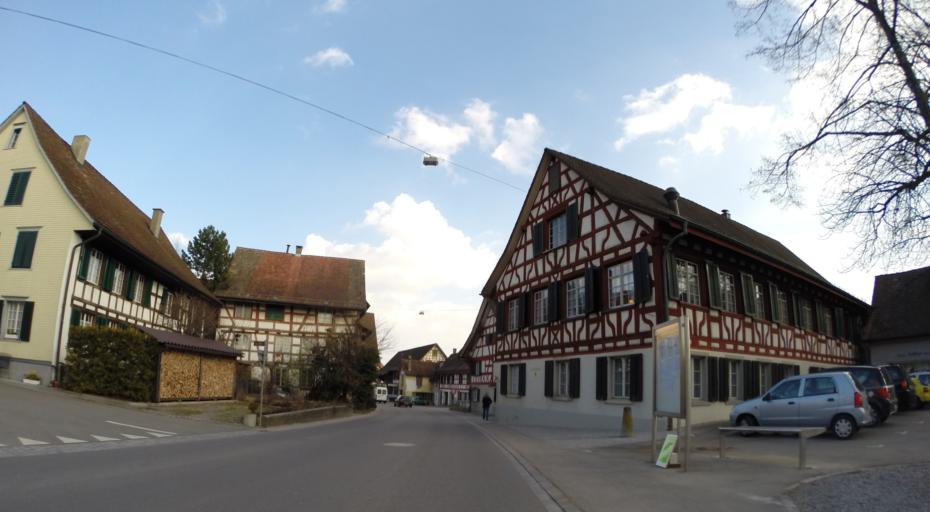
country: CH
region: Thurgau
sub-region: Frauenfeld District
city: Wagenhausen
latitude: 47.6328
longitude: 8.7984
